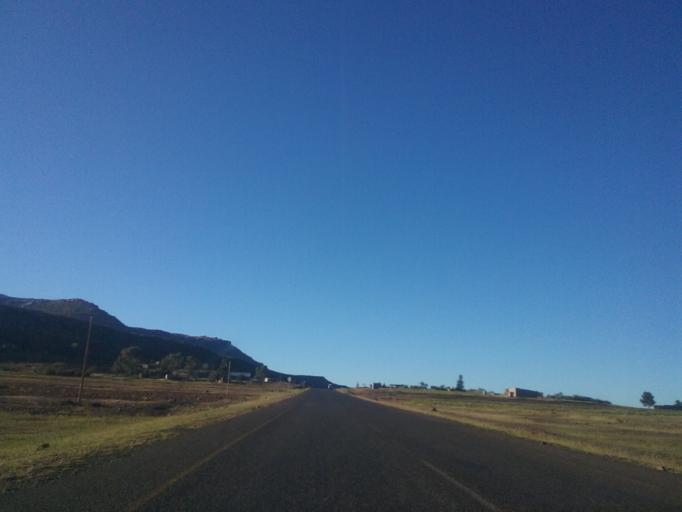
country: LS
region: Mohale's Hoek District
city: Mohale's Hoek
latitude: -30.3081
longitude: 27.5248
